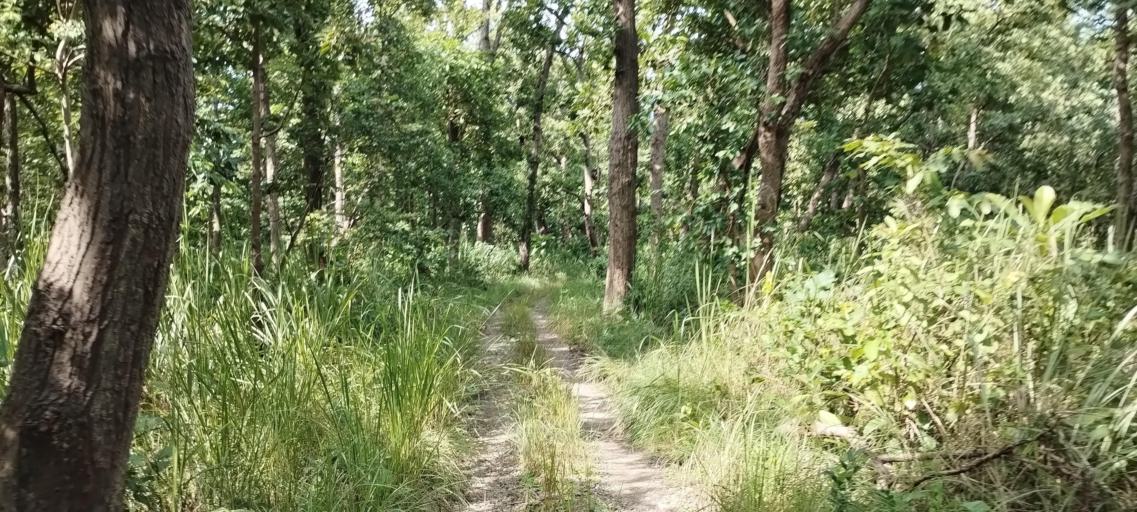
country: NP
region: Far Western
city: Tikapur
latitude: 28.5558
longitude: 81.2924
